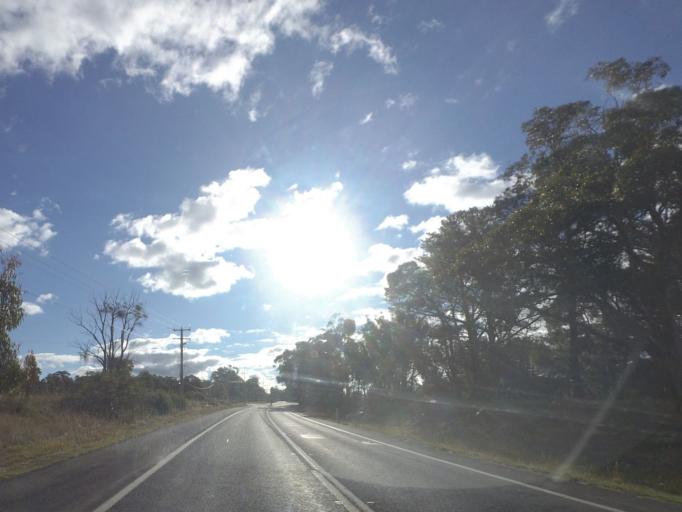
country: AU
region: Victoria
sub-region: Mount Alexander
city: Castlemaine
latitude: -37.0974
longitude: 144.3281
